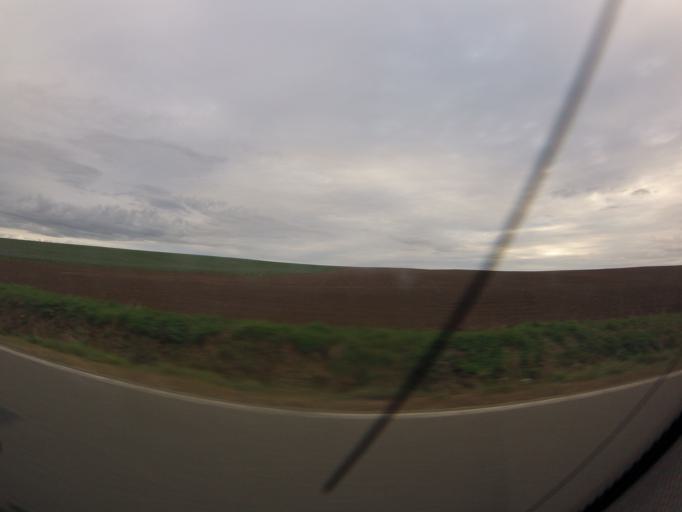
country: DE
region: Thuringia
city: Wildenborten
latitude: 50.8994
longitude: 12.2932
